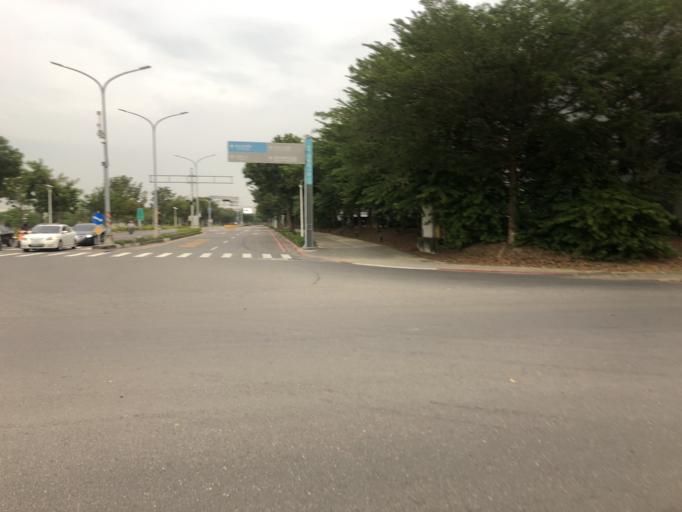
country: TW
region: Taiwan
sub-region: Tainan
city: Tainan
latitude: 23.0827
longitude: 120.2831
